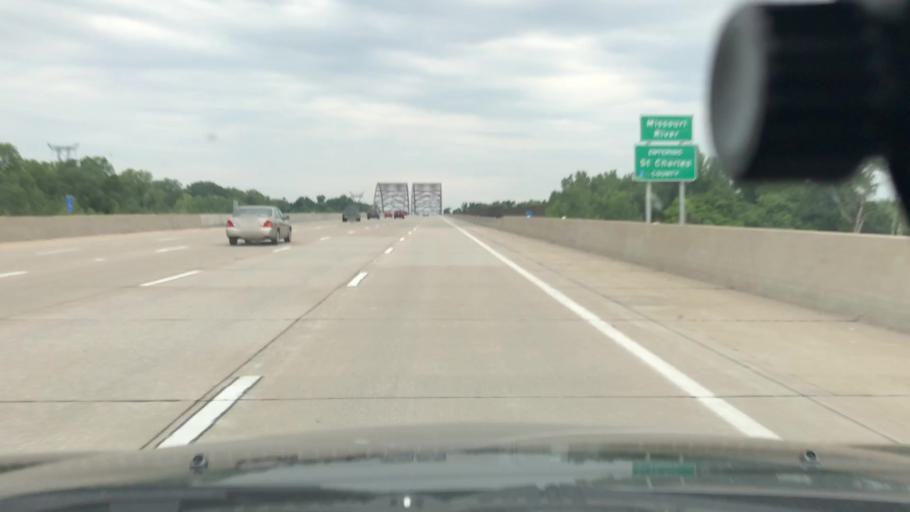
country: US
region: Missouri
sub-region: Saint Charles County
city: Saint Charles
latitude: 38.7306
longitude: -90.5171
